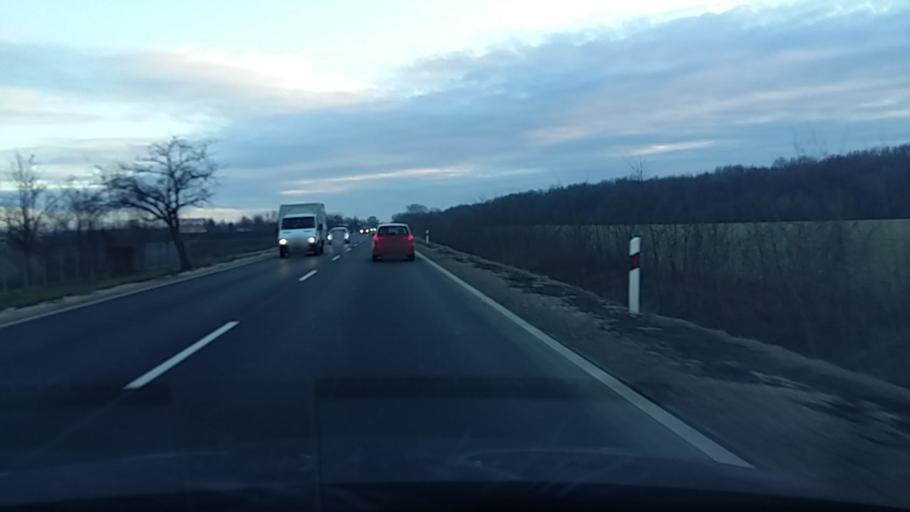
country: HU
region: Hajdu-Bihar
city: Debrecen
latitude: 47.5912
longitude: 21.6541
